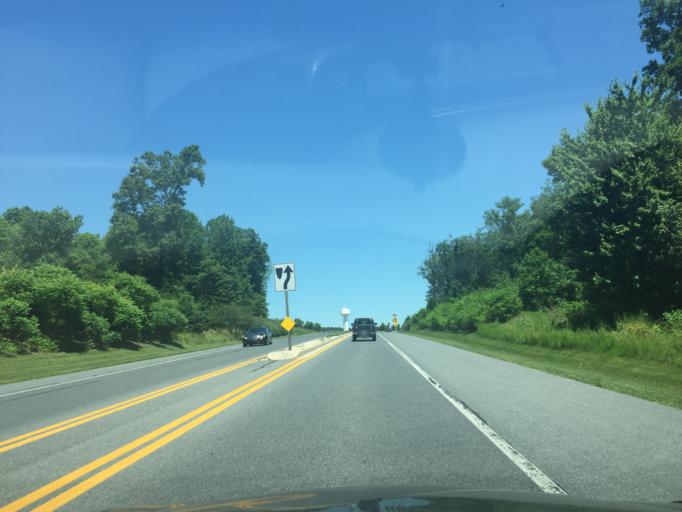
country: US
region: Maryland
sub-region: Carroll County
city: Hampstead
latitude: 39.6305
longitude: -76.8685
